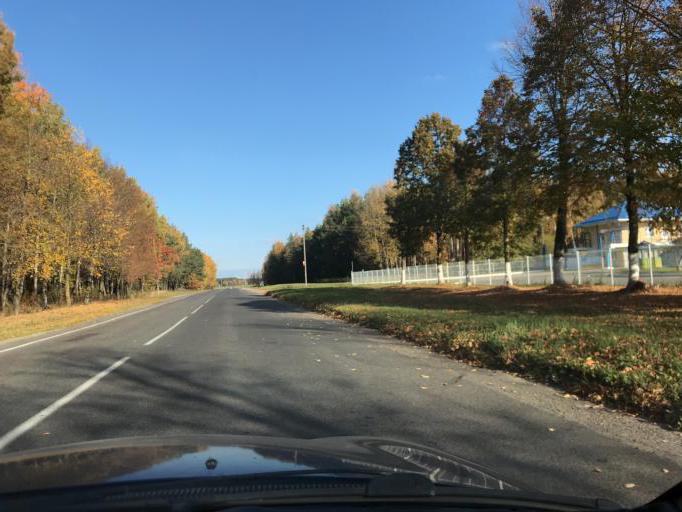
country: BY
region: Grodnenskaya
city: Lida
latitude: 53.9439
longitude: 25.2459
